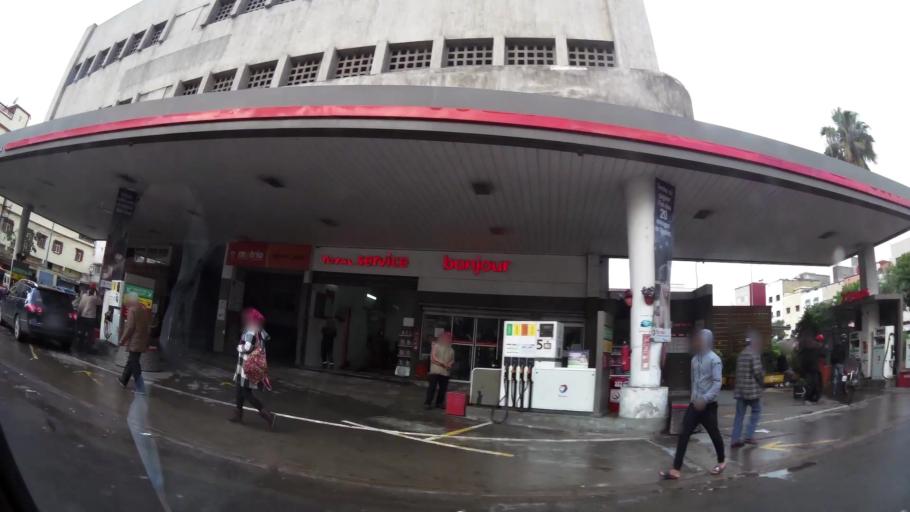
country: MA
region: Grand Casablanca
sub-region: Casablanca
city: Casablanca
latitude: 33.5482
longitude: -7.5731
